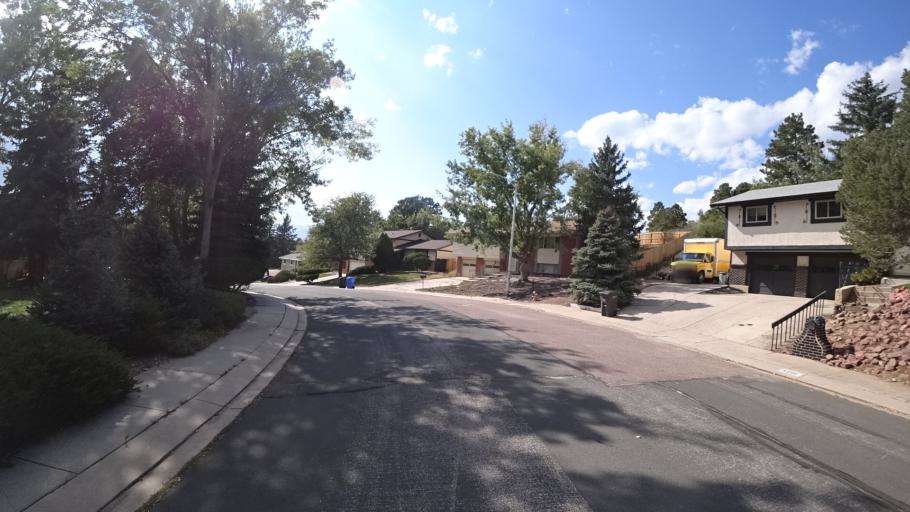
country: US
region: Colorado
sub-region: El Paso County
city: Cimarron Hills
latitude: 38.8721
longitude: -104.7309
